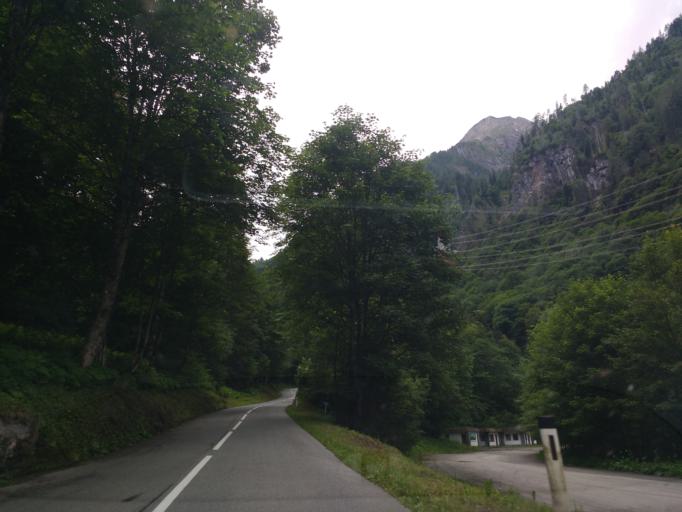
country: AT
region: Salzburg
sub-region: Politischer Bezirk Zell am See
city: Kaprun
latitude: 47.2190
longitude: 12.7279
